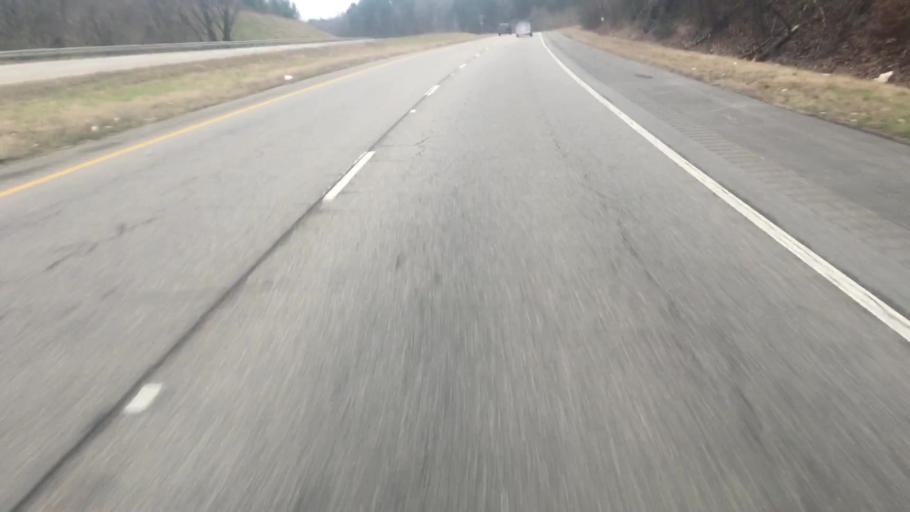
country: US
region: Alabama
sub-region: Walker County
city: Cordova
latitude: 33.8125
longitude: -87.1478
